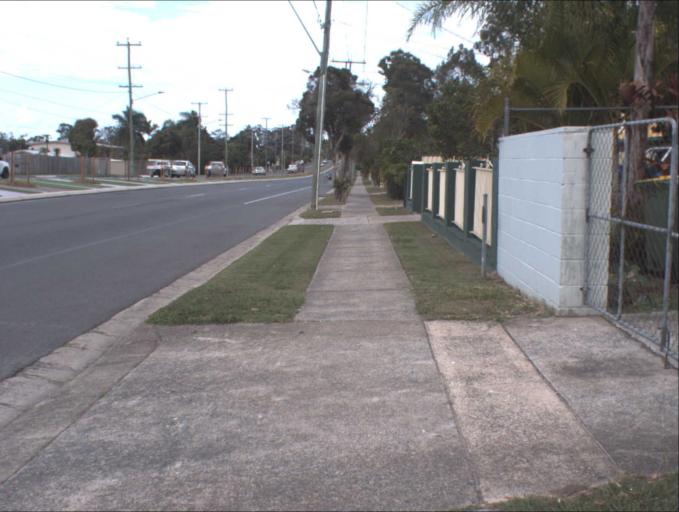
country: AU
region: Queensland
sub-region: Logan
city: Waterford West
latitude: -27.6814
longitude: 153.0939
